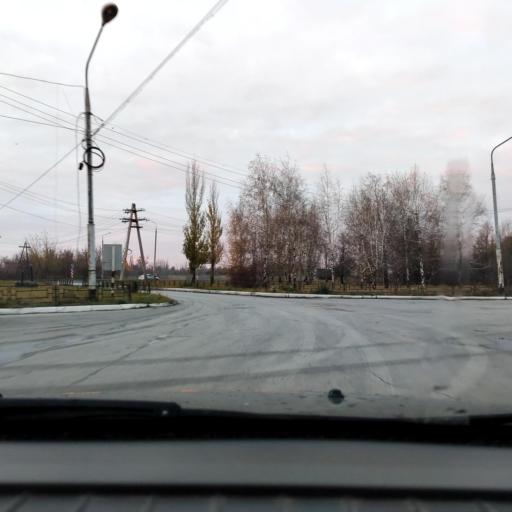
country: RU
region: Samara
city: Tol'yatti
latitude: 53.5583
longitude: 49.3304
